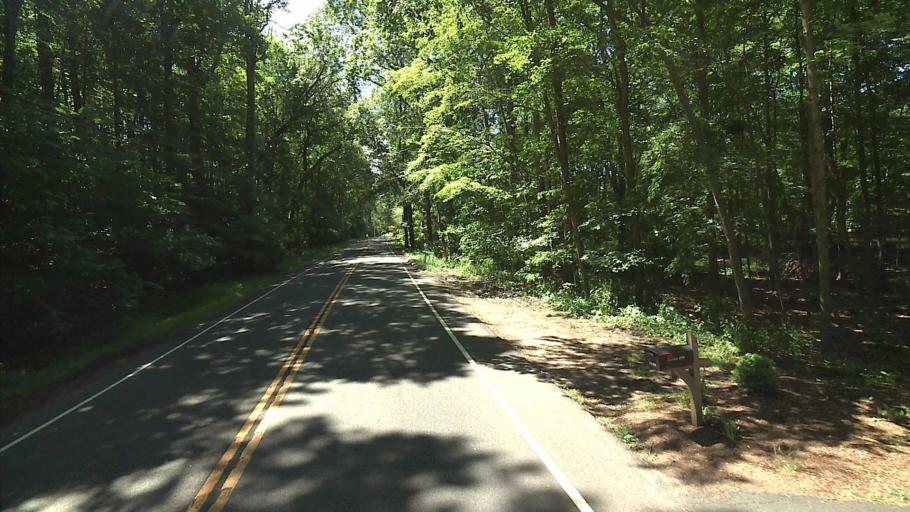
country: US
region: Connecticut
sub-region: New Haven County
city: North Branford
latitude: 41.3451
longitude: -72.7159
